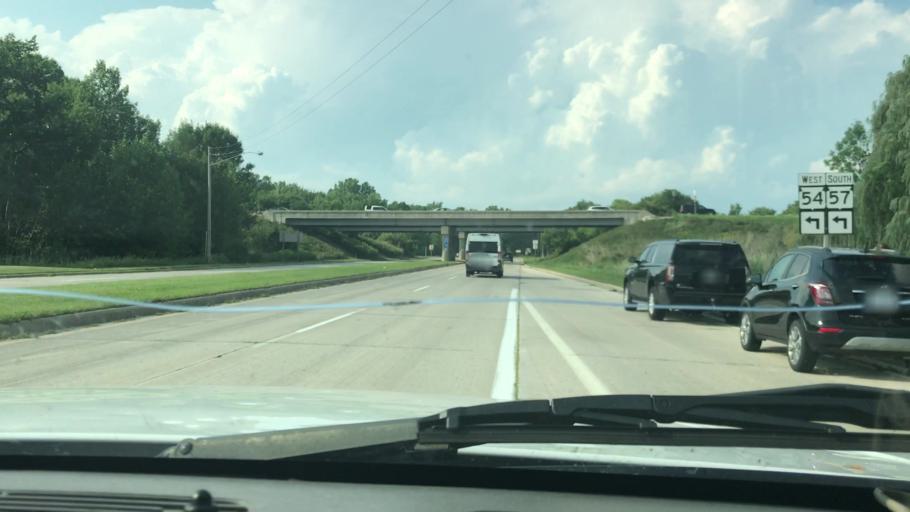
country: US
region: Wisconsin
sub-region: Brown County
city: Green Bay
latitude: 44.5239
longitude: -87.9407
